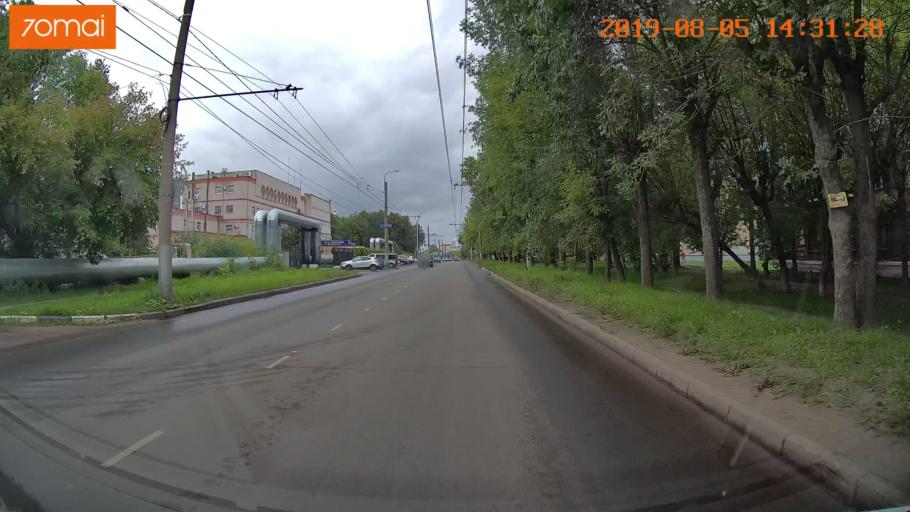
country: RU
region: Ivanovo
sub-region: Gorod Ivanovo
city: Ivanovo
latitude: 56.9869
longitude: 41.0019
